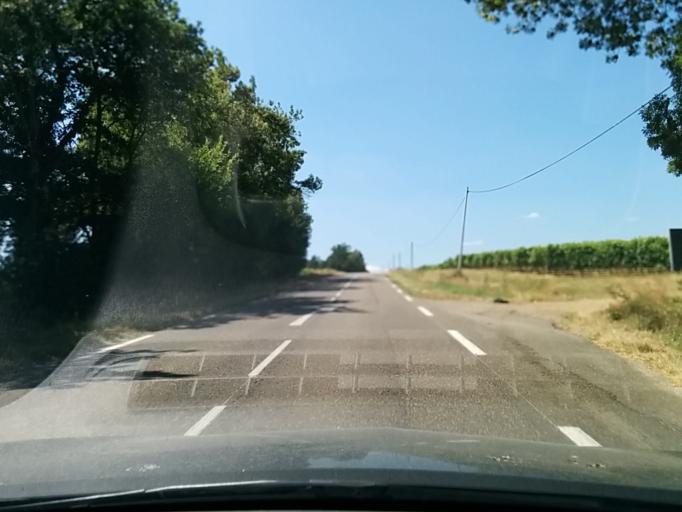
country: FR
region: Midi-Pyrenees
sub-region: Departement du Gers
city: Nogaro
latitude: 43.7541
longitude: -0.0950
